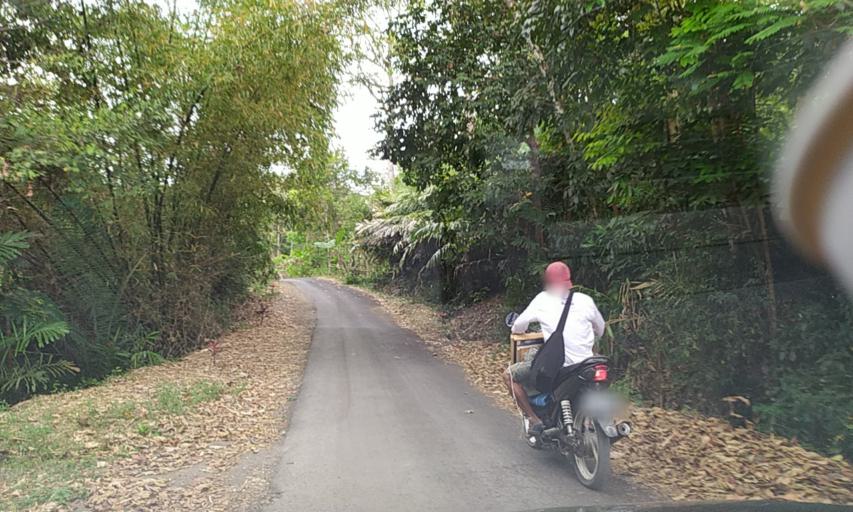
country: ID
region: Central Java
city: Batububut
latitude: -7.2936
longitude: 108.5773
